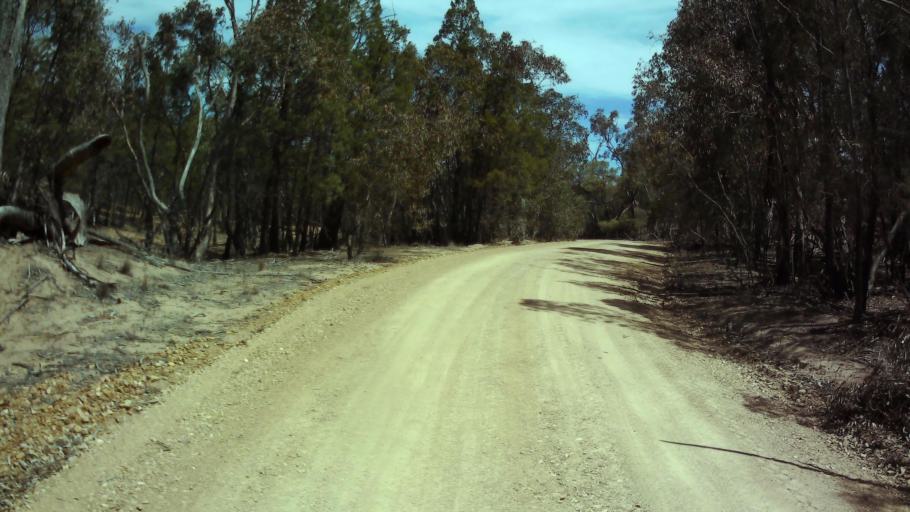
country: AU
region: New South Wales
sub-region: Weddin
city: Grenfell
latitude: -33.8057
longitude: 148.1605
